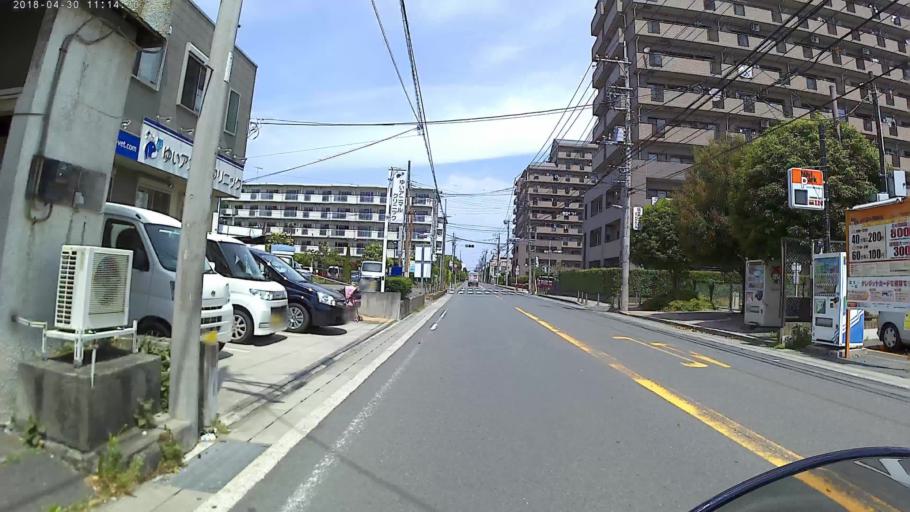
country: JP
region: Kanagawa
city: Minami-rinkan
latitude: 35.4745
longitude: 139.4315
